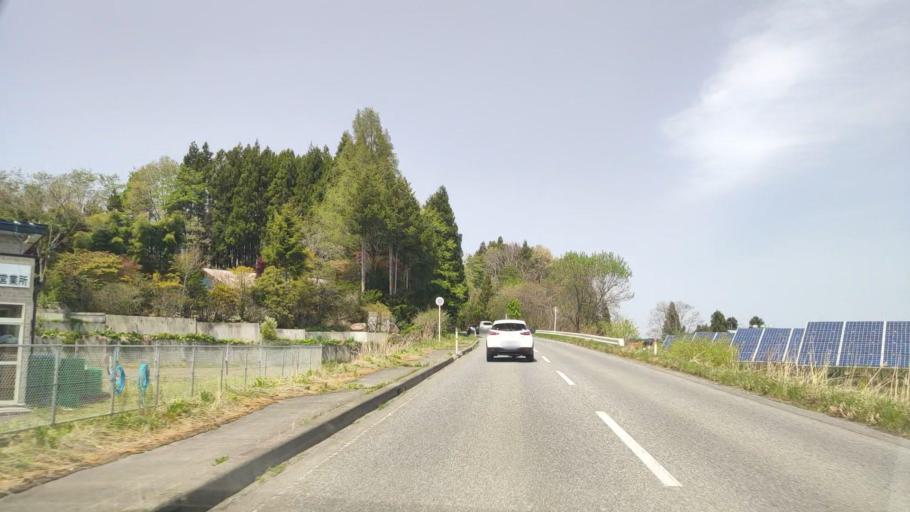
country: JP
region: Aomori
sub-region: Misawa Shi
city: Inuotose
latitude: 40.5884
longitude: 141.3522
